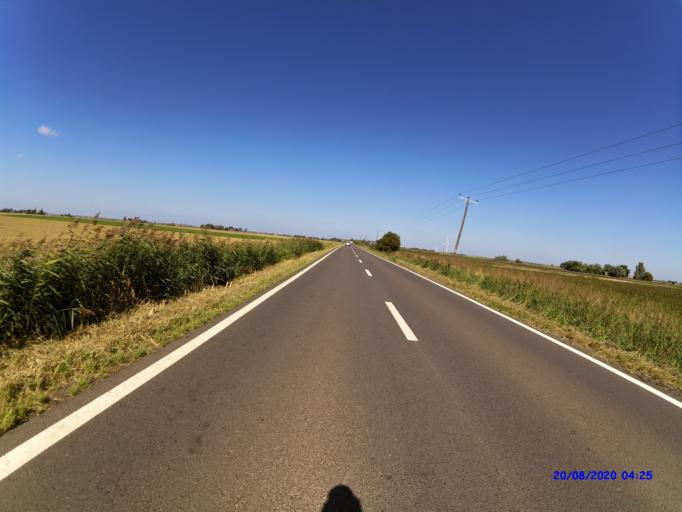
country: GB
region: England
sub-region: Cambridgeshire
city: Ramsey
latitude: 52.5004
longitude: -0.1291
